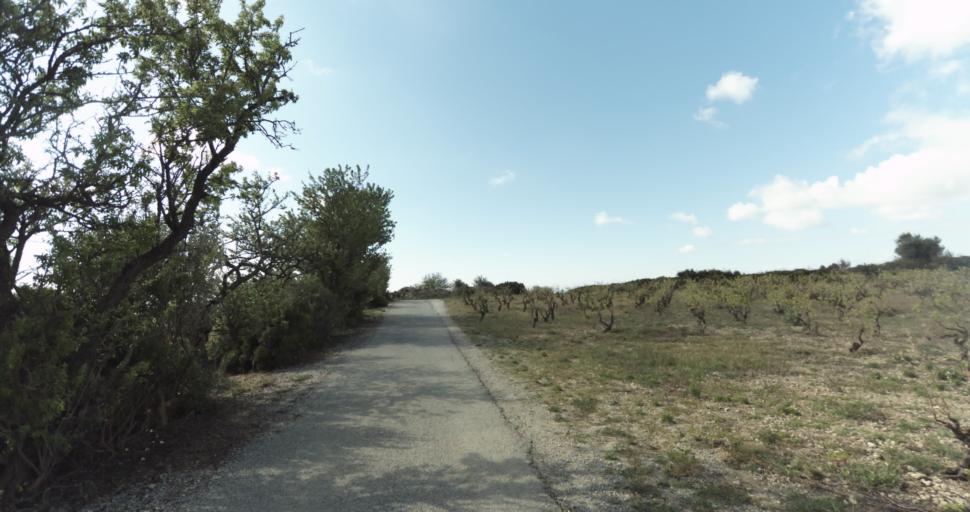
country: FR
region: Languedoc-Roussillon
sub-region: Departement de l'Aude
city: Leucate
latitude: 42.9220
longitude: 3.0365
